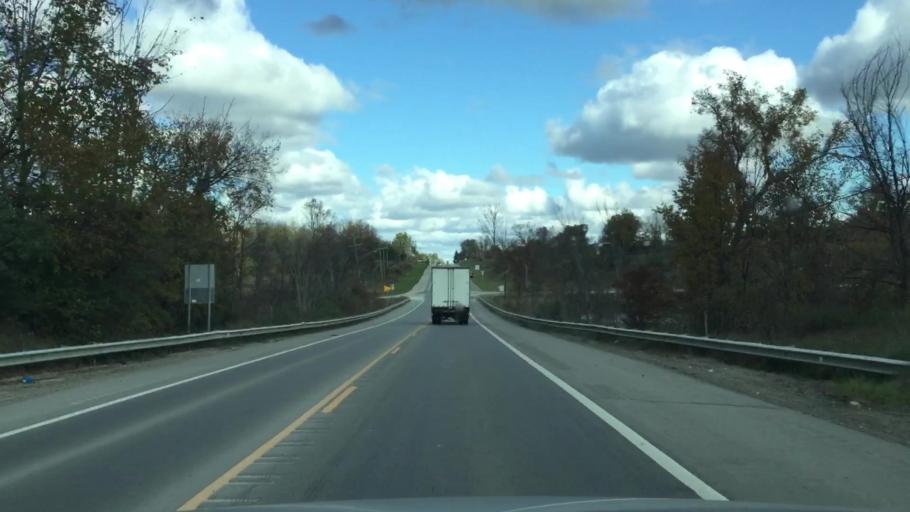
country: US
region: Michigan
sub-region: Oakland County
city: Oxford
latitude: 42.9105
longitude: -83.3123
